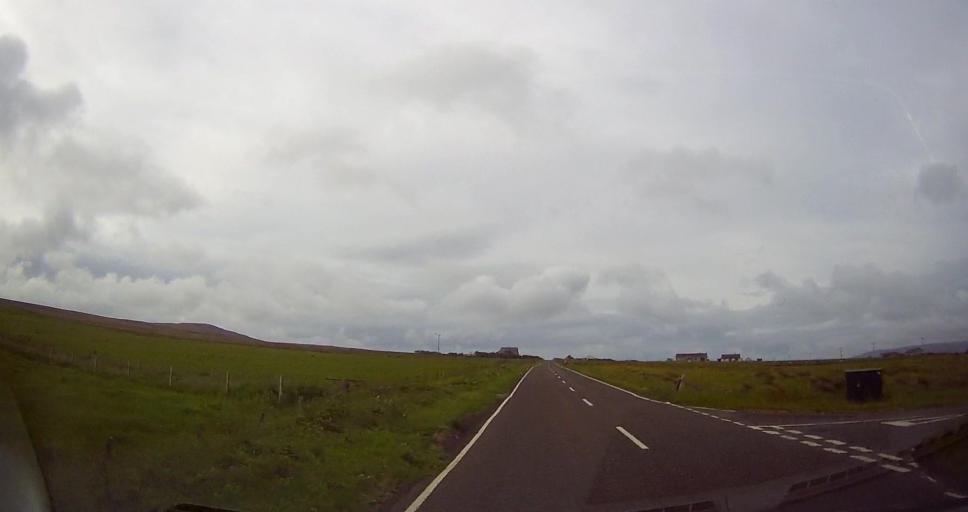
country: GB
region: Scotland
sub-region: Orkney Islands
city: Stromness
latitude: 58.9586
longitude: -3.2212
